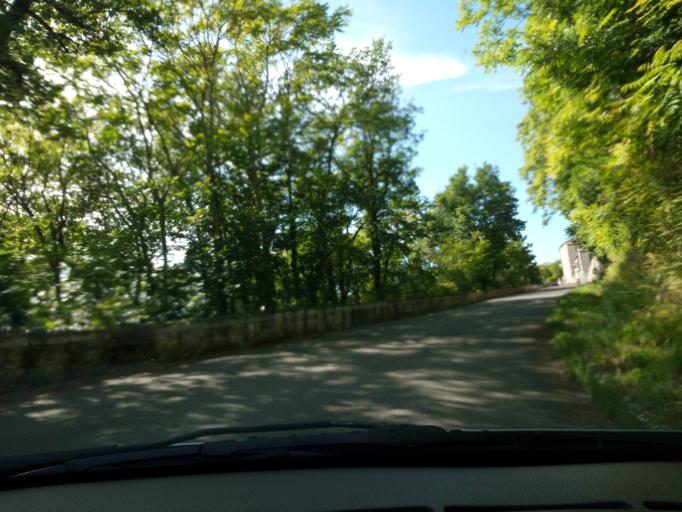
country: FR
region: Midi-Pyrenees
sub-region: Departement du Lot
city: Castelnau-Montratier
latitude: 44.2656
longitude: 1.3546
